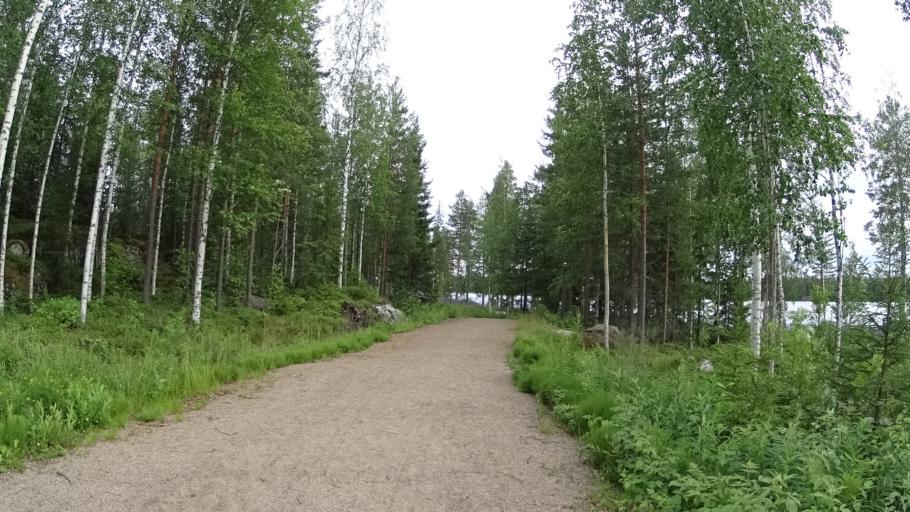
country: FI
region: Southern Ostrobothnia
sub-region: Kuusiokunnat
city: AEhtaeri
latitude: 62.5318
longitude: 24.1873
